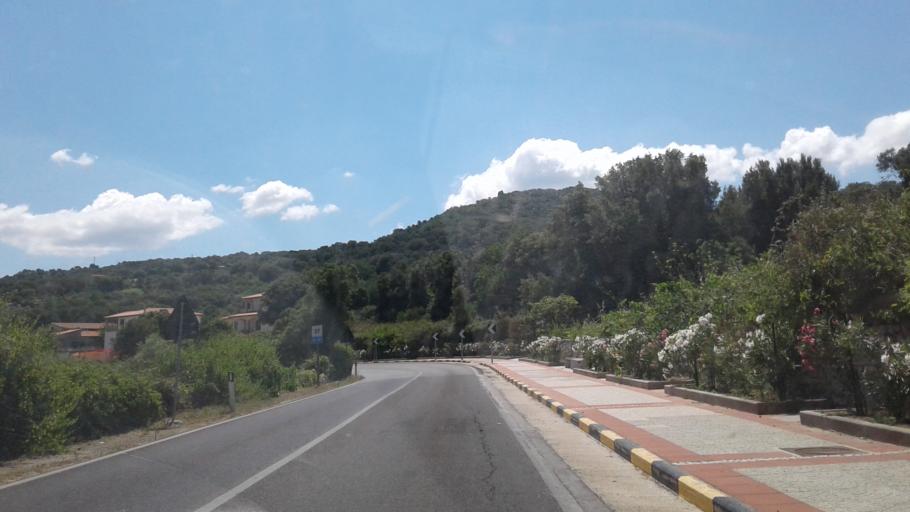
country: IT
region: Sardinia
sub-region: Provincia di Olbia-Tempio
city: Calangianus
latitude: 40.9217
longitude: 9.1817
